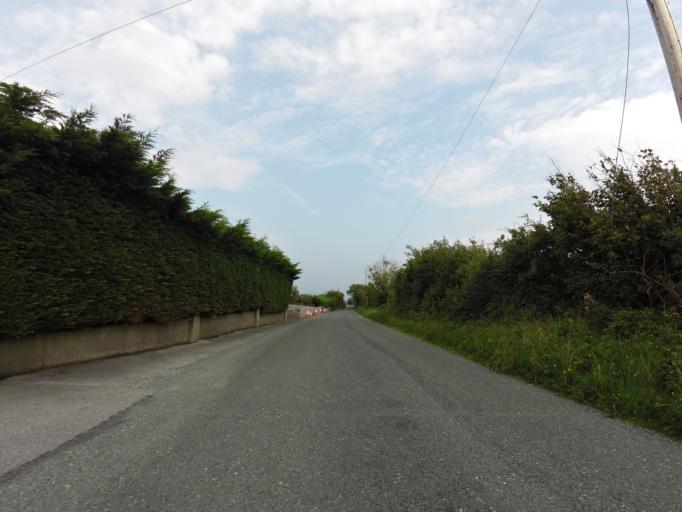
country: IE
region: Connaught
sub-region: County Galway
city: Gaillimh
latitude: 53.3146
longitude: -9.0493
